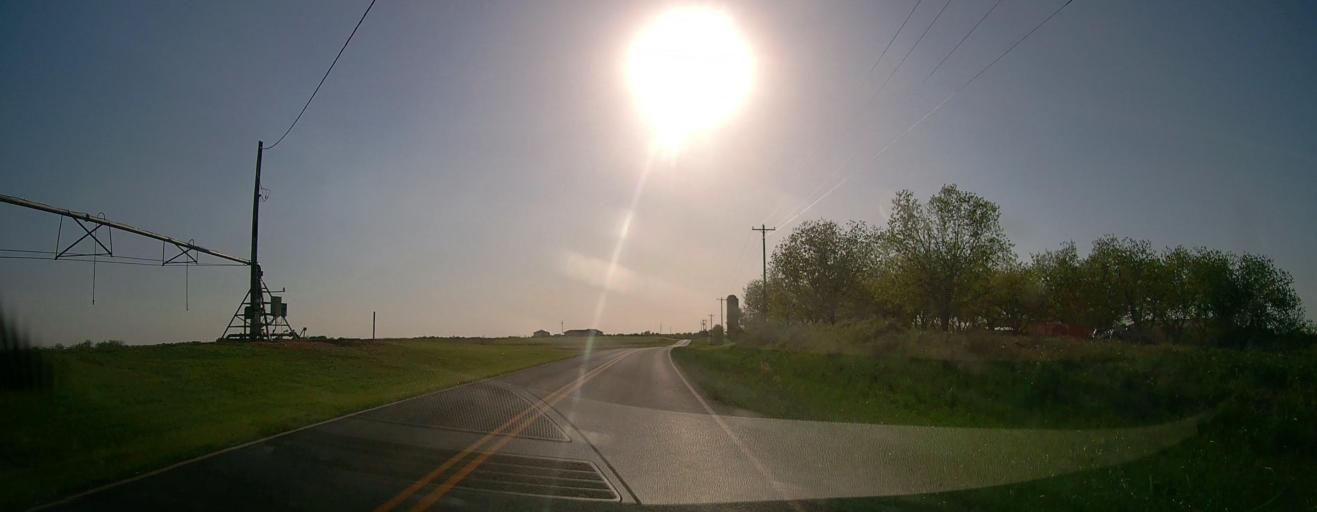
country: US
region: Georgia
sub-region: Macon County
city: Montezuma
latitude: 32.3179
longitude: -83.9763
